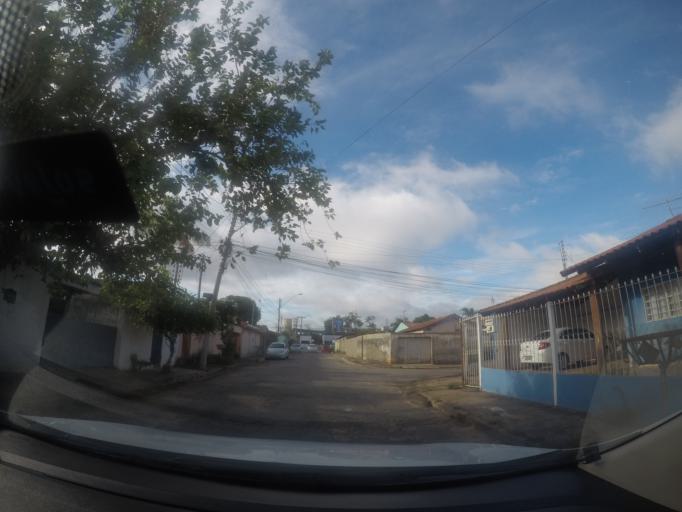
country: BR
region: Goias
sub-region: Goiania
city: Goiania
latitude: -16.6896
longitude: -49.3137
